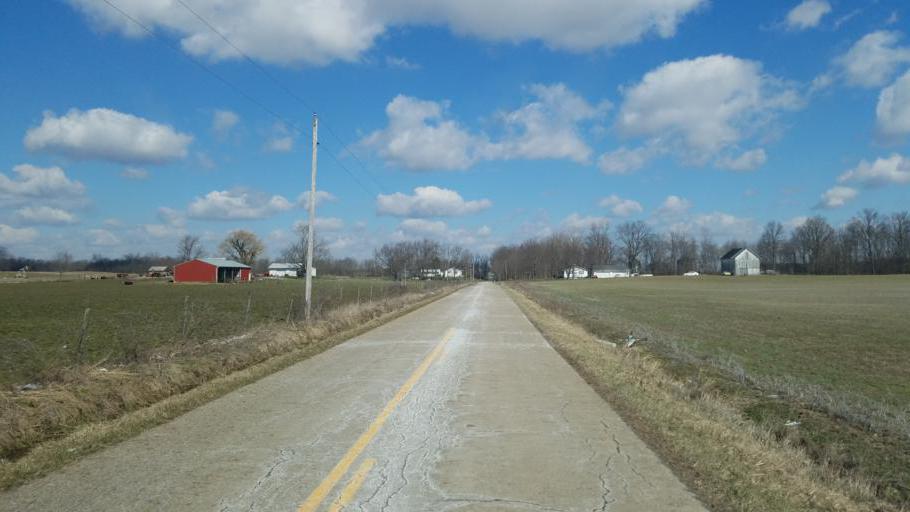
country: US
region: Ohio
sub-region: Licking County
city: Utica
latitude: 40.2787
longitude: -82.5451
